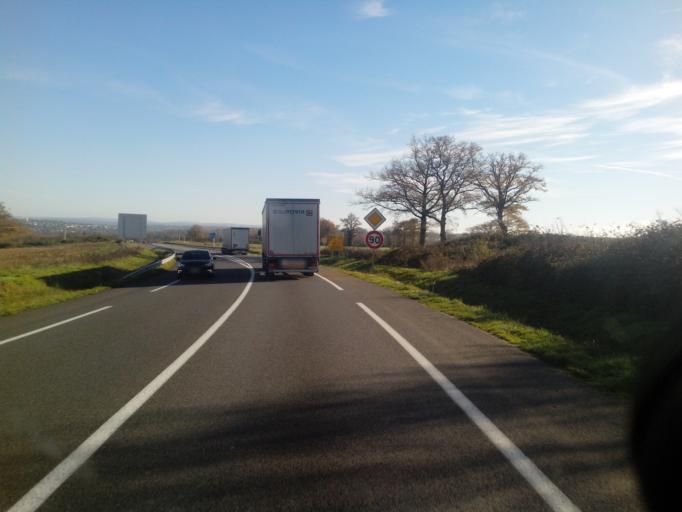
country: FR
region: Limousin
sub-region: Departement de la Haute-Vienne
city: Peyrat-de-Bellac
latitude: 46.1290
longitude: 0.9923
